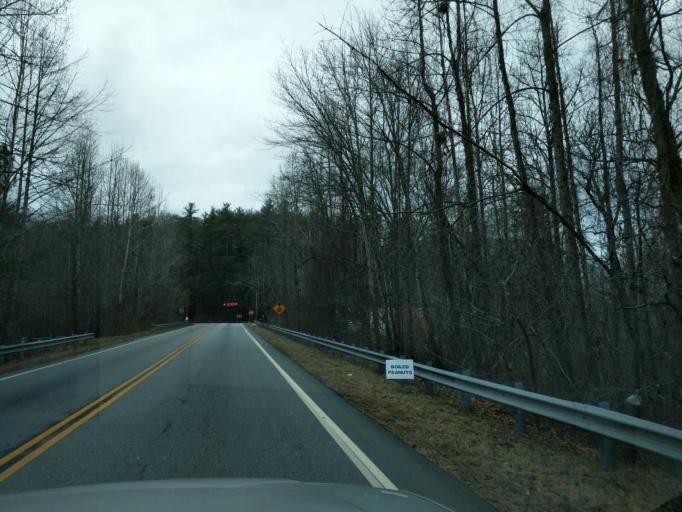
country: US
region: South Carolina
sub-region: Greenville County
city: Slater-Marietta
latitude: 35.0711
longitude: -82.5152
